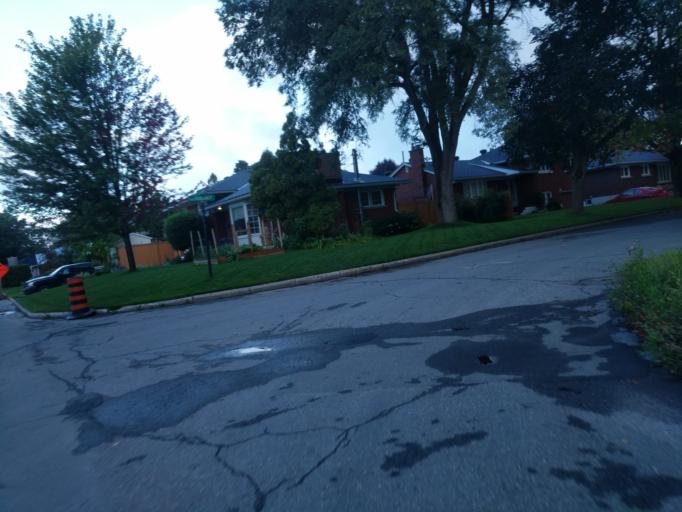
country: CA
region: Ontario
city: Ottawa
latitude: 45.3634
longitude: -75.7536
